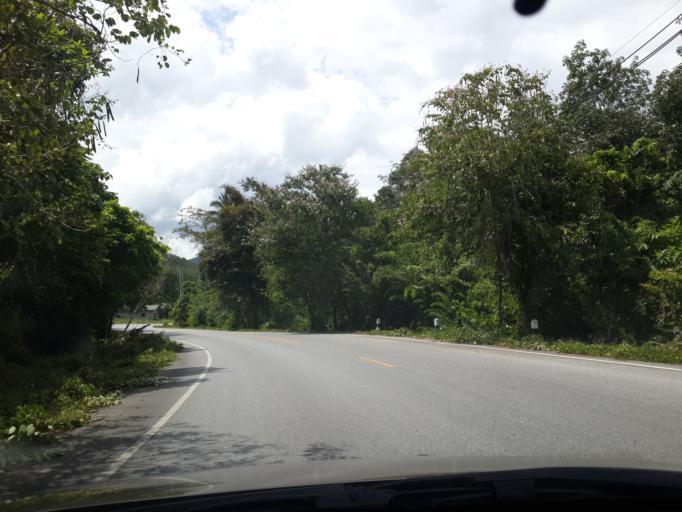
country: TH
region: Narathiwat
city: Rueso
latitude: 6.3789
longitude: 101.4234
